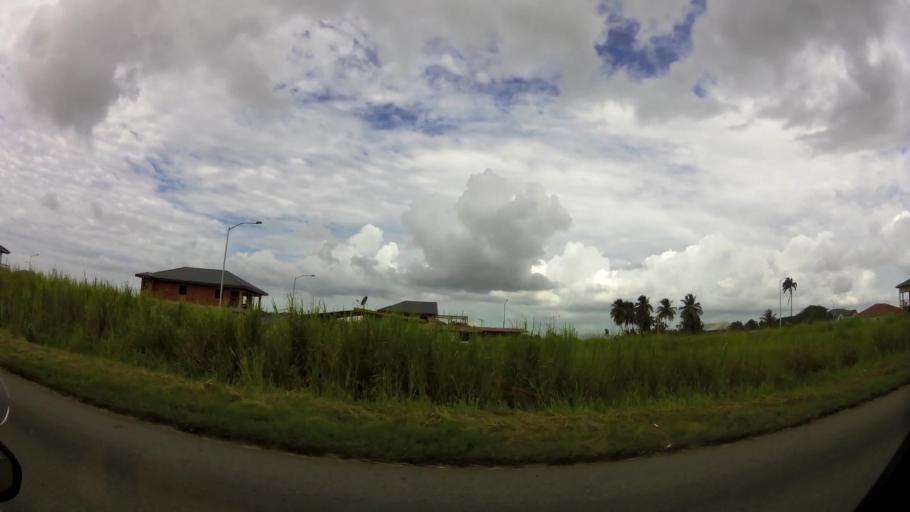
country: TT
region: Couva-Tabaquite-Talparo
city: Couva
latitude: 10.4515
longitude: -61.4396
